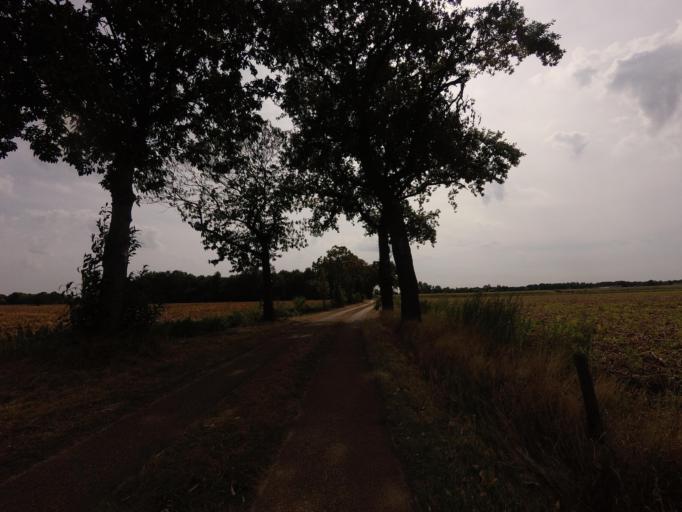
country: NL
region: North Brabant
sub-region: Gemeente Helmond
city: Helmond
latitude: 51.4900
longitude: 5.7234
